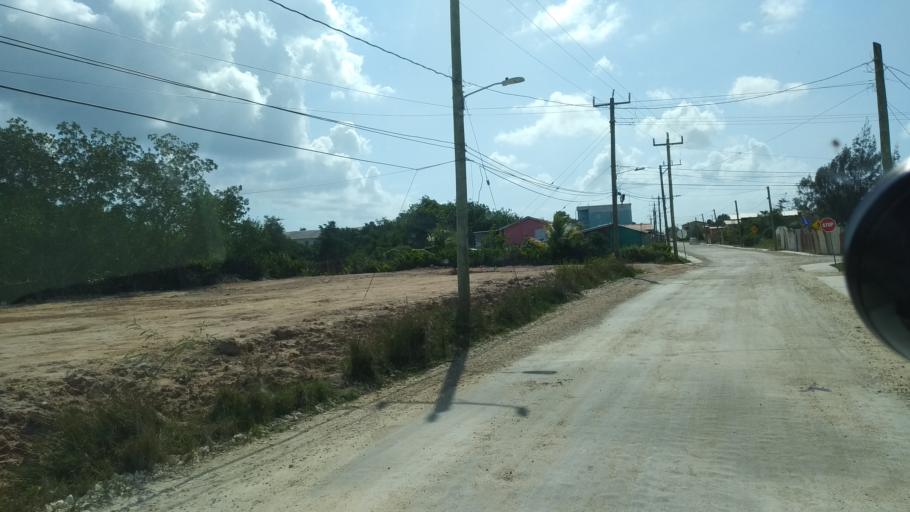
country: BZ
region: Belize
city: Belize City
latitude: 17.5170
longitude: -88.2330
